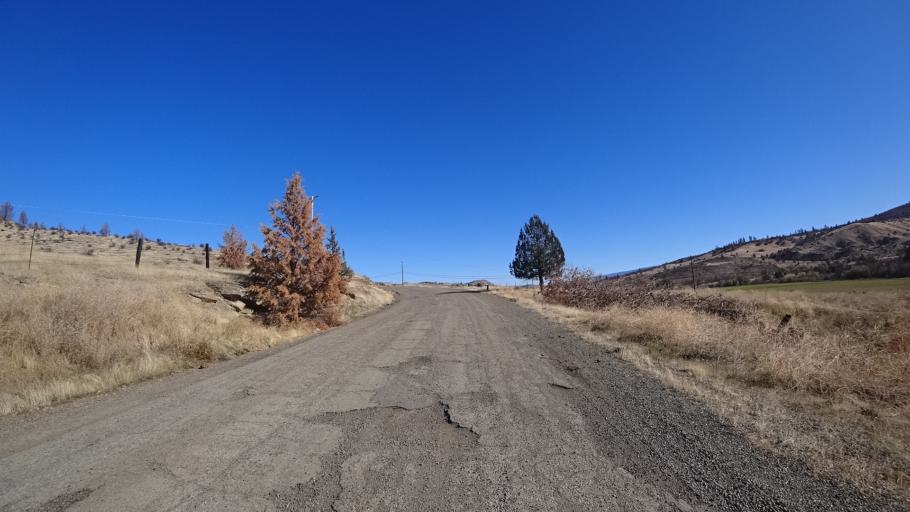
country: US
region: California
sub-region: Siskiyou County
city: Montague
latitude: 41.8892
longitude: -122.5512
